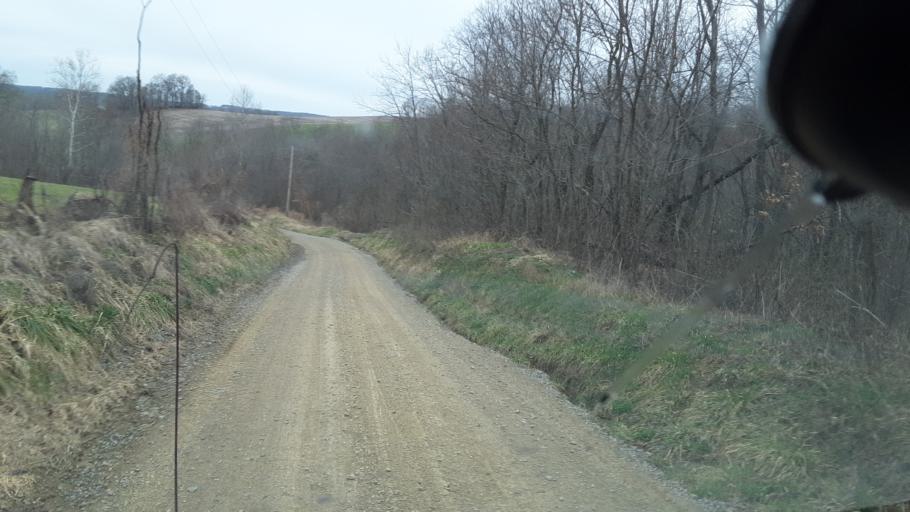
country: US
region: Ohio
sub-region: Coshocton County
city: West Lafayette
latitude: 40.3395
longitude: -81.7102
